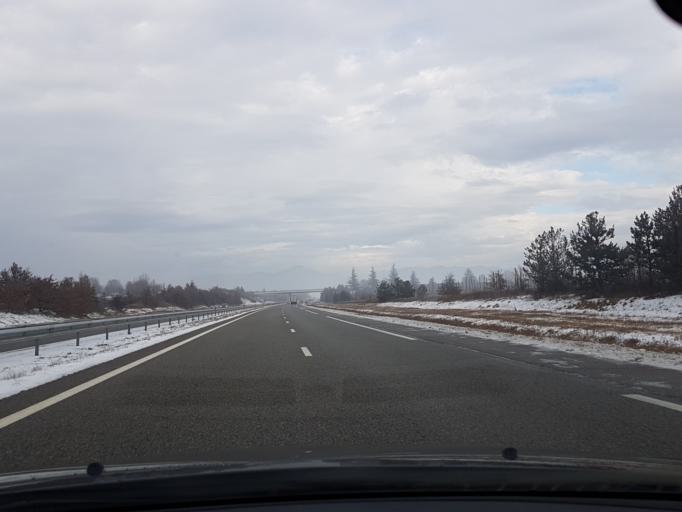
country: FR
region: Provence-Alpes-Cote d'Azur
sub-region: Departement des Alpes-de-Haute-Provence
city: Sisteron
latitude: 44.2487
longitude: 5.9108
